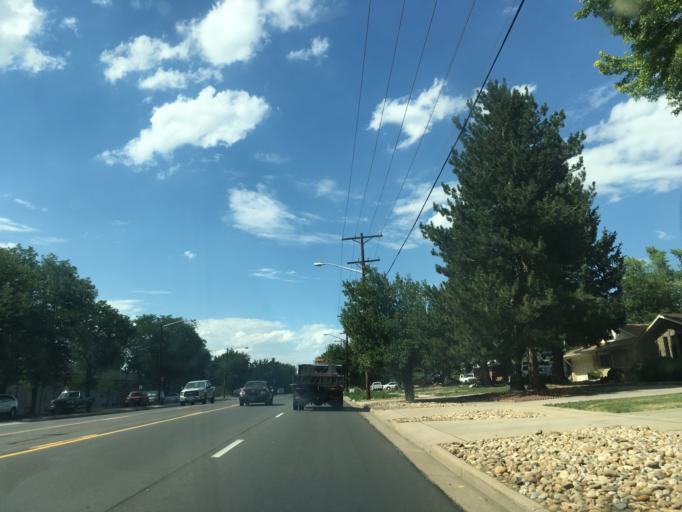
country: US
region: Colorado
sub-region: Arapahoe County
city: Sheridan
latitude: 39.6701
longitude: -105.0532
